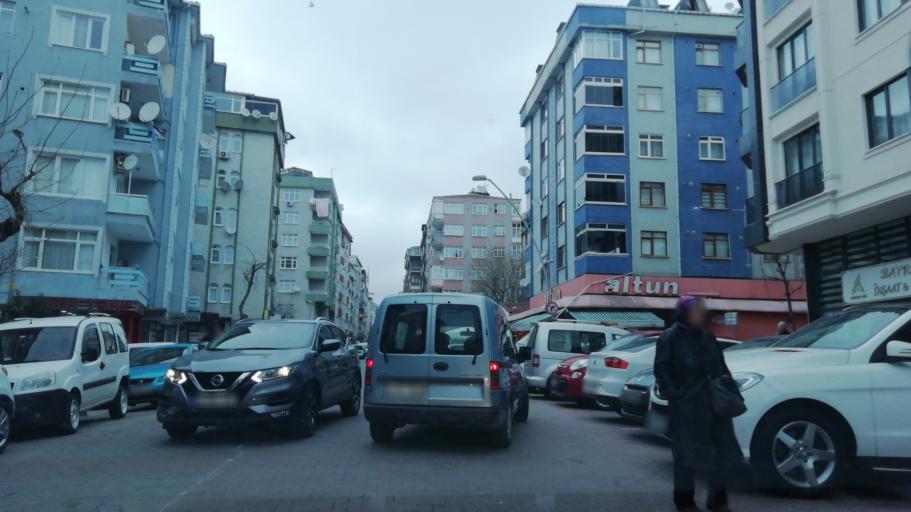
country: TR
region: Istanbul
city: Bahcelievler
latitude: 41.0008
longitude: 28.8549
